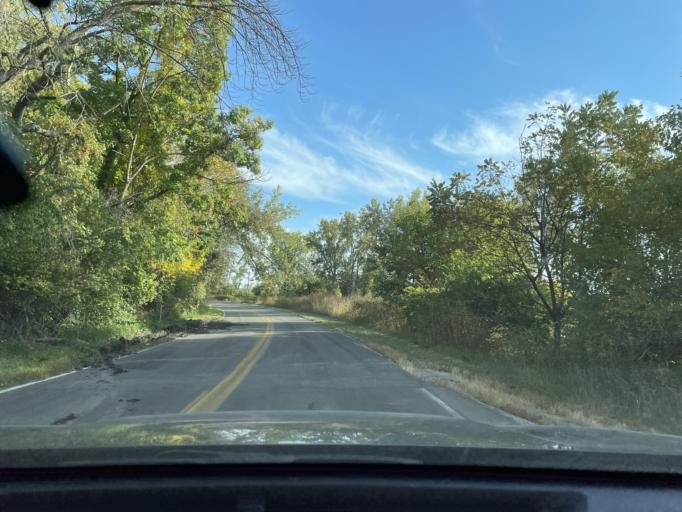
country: US
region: Kansas
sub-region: Doniphan County
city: Elwood
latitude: 39.7780
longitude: -94.8698
